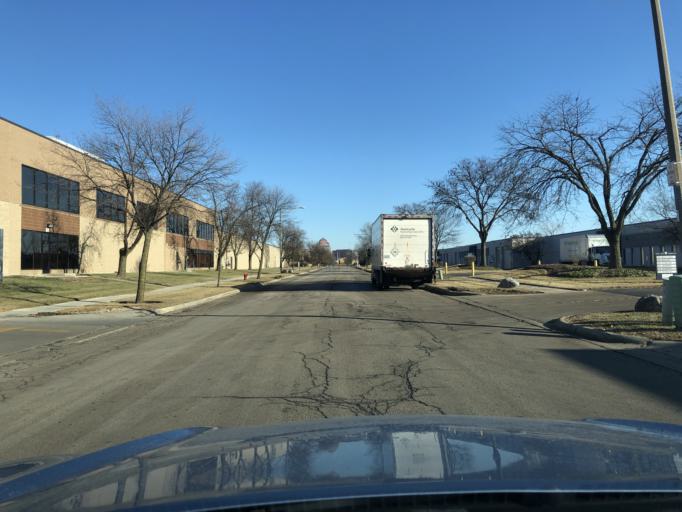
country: US
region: Illinois
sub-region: DuPage County
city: Itasca
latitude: 41.9859
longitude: -88.0393
